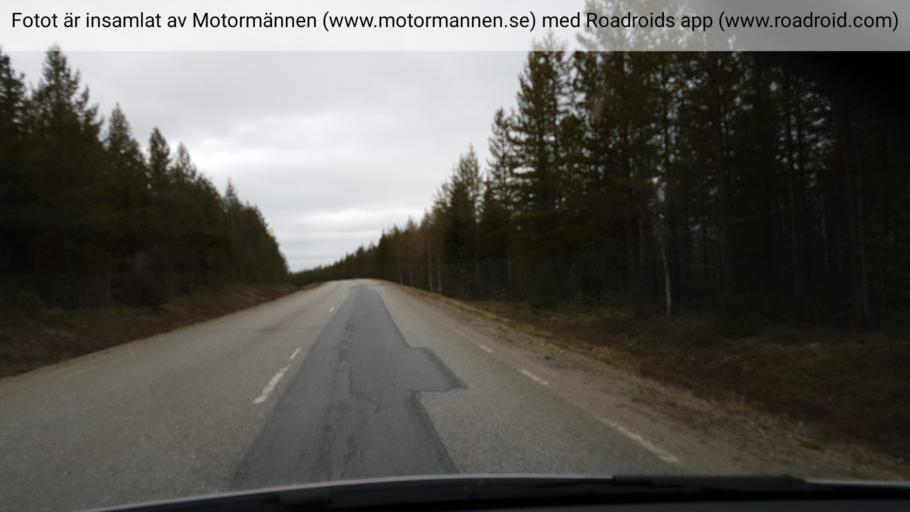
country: SE
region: Vaesterbotten
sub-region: Lycksele Kommun
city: Lycksele
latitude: 64.0528
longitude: 18.4241
